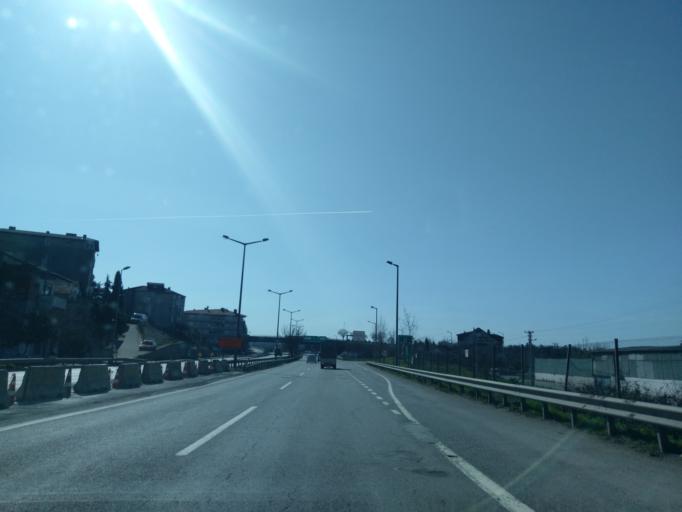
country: TR
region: Kocaeli
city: Darica
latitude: 40.8200
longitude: 29.3647
